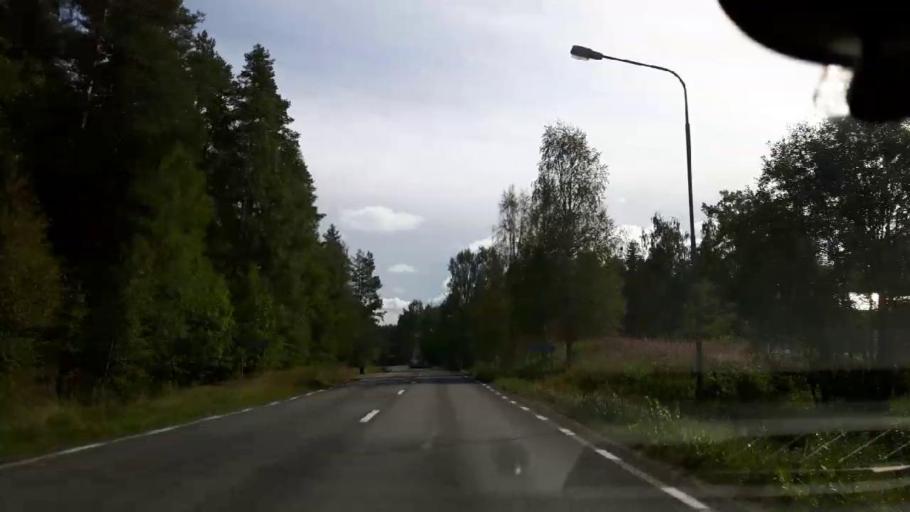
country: SE
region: Jaemtland
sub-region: Braecke Kommun
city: Braecke
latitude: 63.1657
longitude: 15.5591
